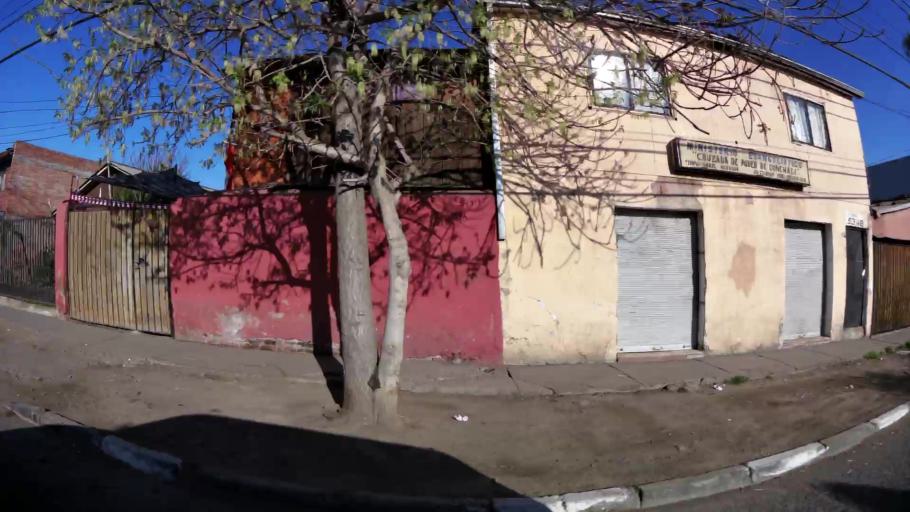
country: CL
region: Santiago Metropolitan
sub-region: Provincia de Santiago
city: Santiago
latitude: -33.3789
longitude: -70.6693
